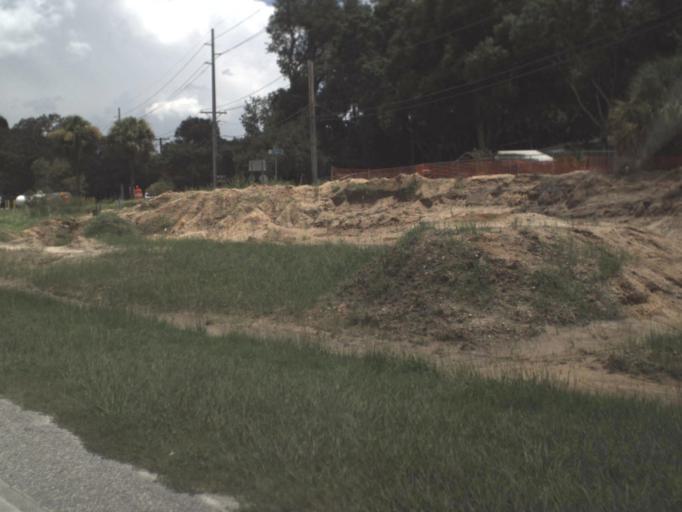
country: US
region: Florida
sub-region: Hillsborough County
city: Thonotosassa
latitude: 28.0546
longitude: -82.3292
